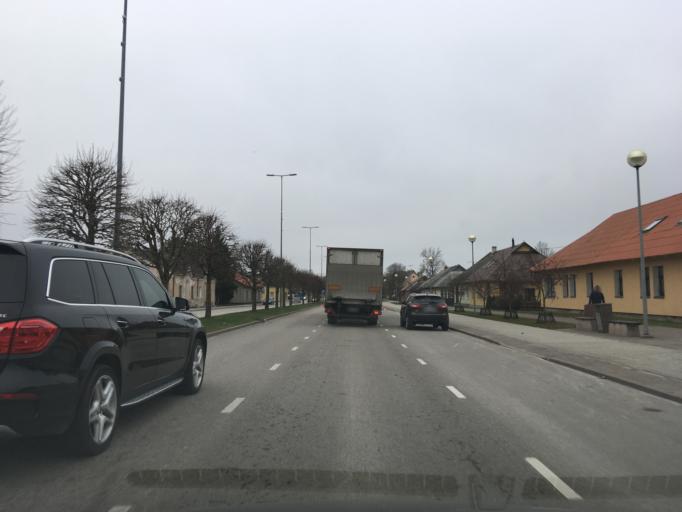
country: EE
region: Ida-Virumaa
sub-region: Johvi vald
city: Johvi
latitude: 59.3606
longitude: 27.4057
